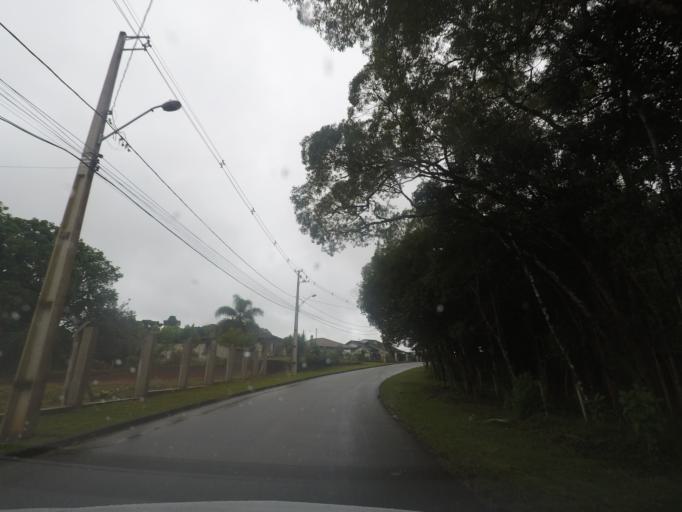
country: BR
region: Parana
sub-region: Campina Grande Do Sul
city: Campina Grande do Sul
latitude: -25.3055
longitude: -49.1351
